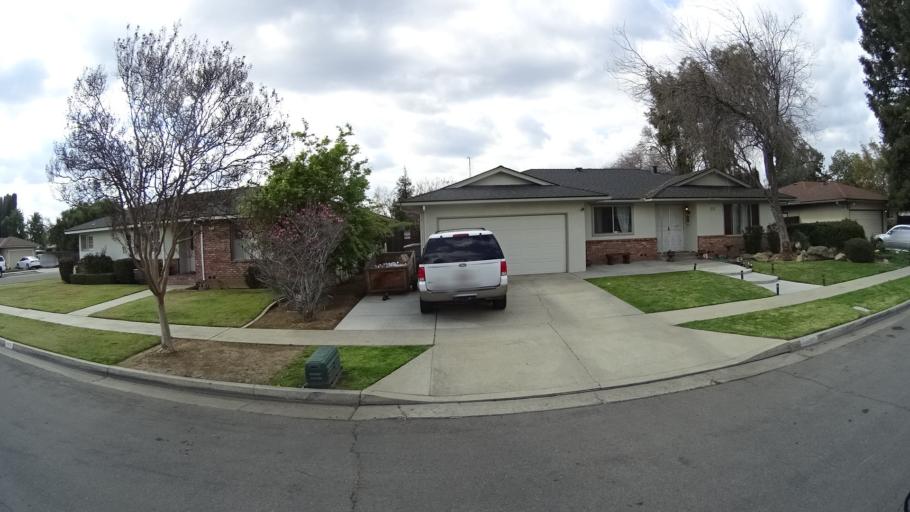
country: US
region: California
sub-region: Fresno County
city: Clovis
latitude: 36.8336
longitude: -119.7763
